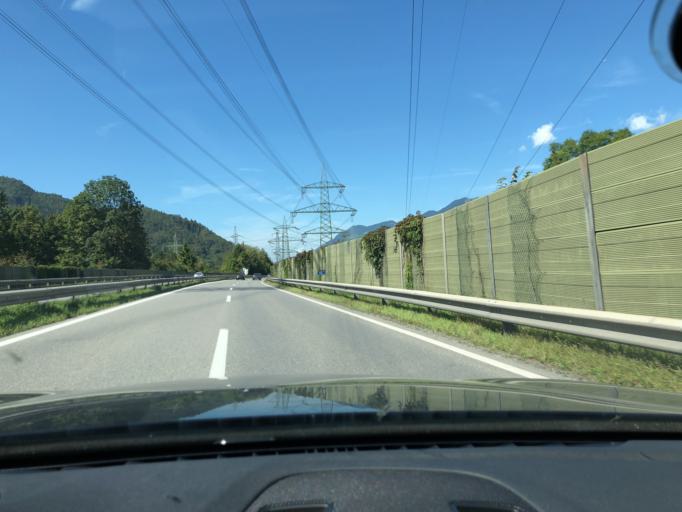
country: AT
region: Vorarlberg
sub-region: Politischer Bezirk Bludenz
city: Buers
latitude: 47.1541
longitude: 9.8103
